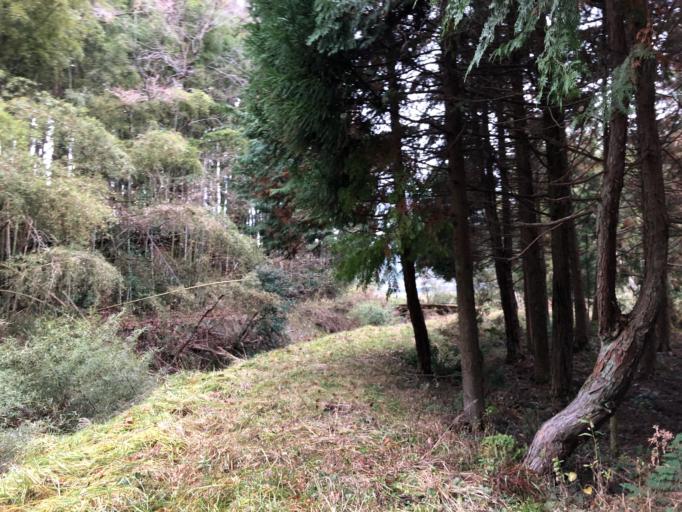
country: JP
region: Kyoto
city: Kameoka
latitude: 34.9913
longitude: 135.6208
